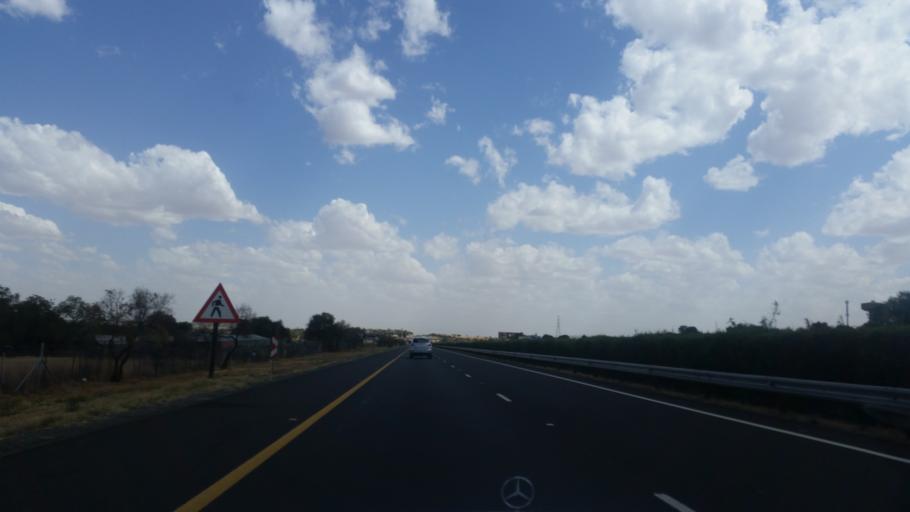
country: ZA
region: Orange Free State
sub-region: Mangaung Metropolitan Municipality
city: Bloemfontein
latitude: -29.0798
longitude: 26.1787
